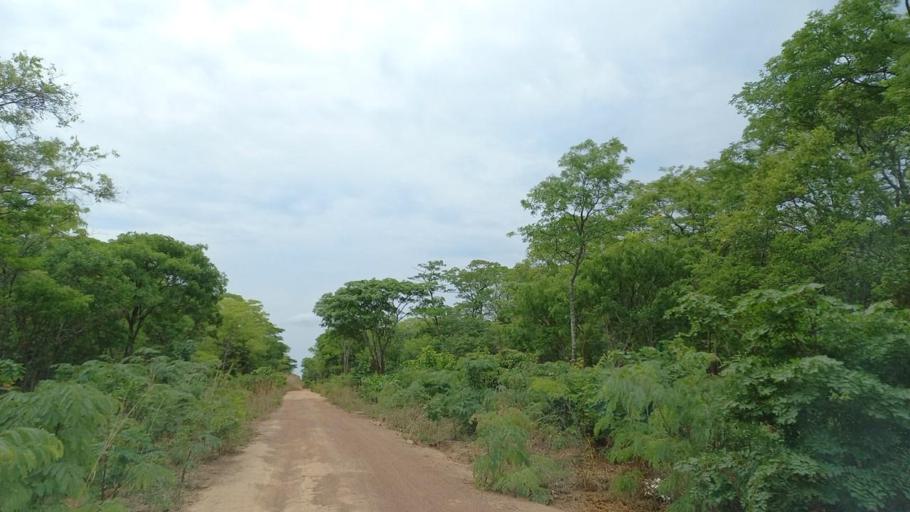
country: ZM
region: North-Western
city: Kalengwa
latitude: -13.5917
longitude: 24.9728
